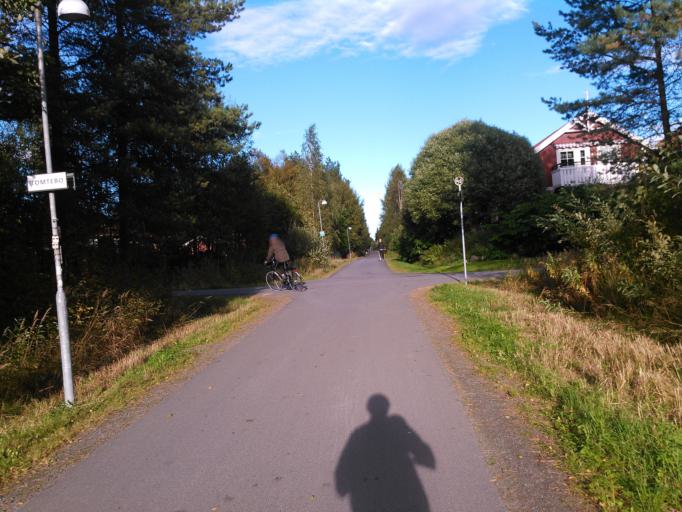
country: SE
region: Vaesterbotten
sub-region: Umea Kommun
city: Ersmark
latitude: 63.8090
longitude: 20.3351
